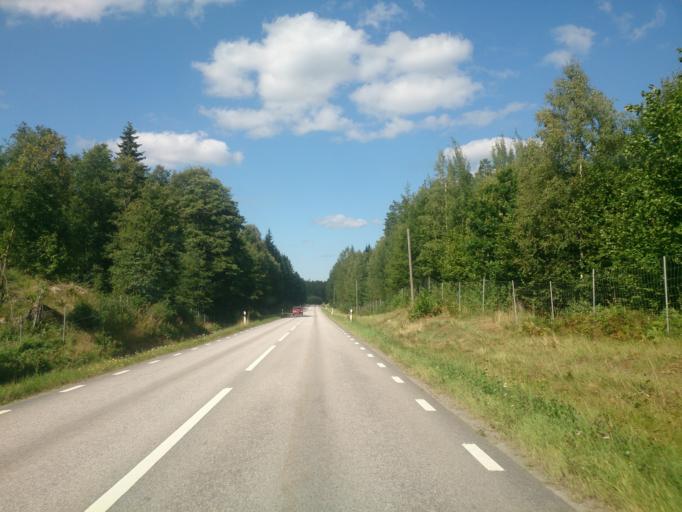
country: SE
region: OEstergoetland
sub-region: Atvidabergs Kommun
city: Atvidaberg
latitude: 58.1724
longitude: 16.0366
